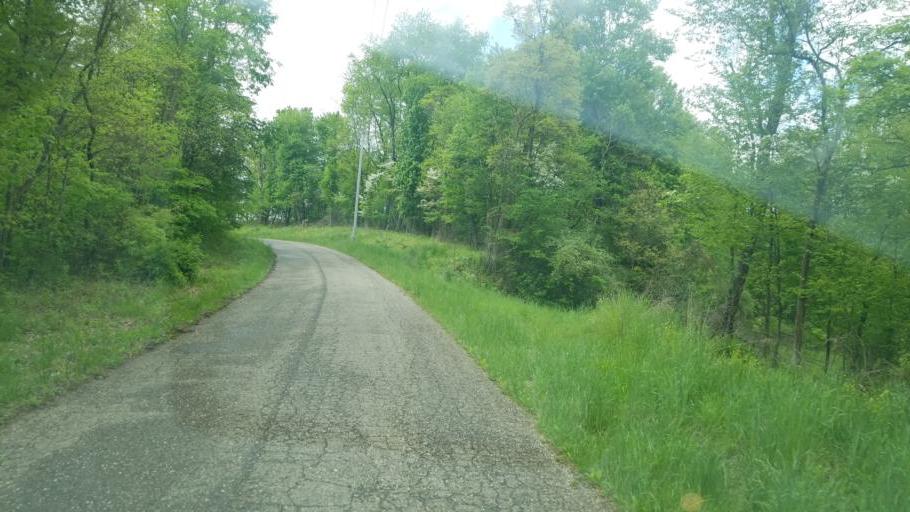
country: US
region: Ohio
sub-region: Tuscarawas County
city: Rockford
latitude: 40.4541
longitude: -81.2746
